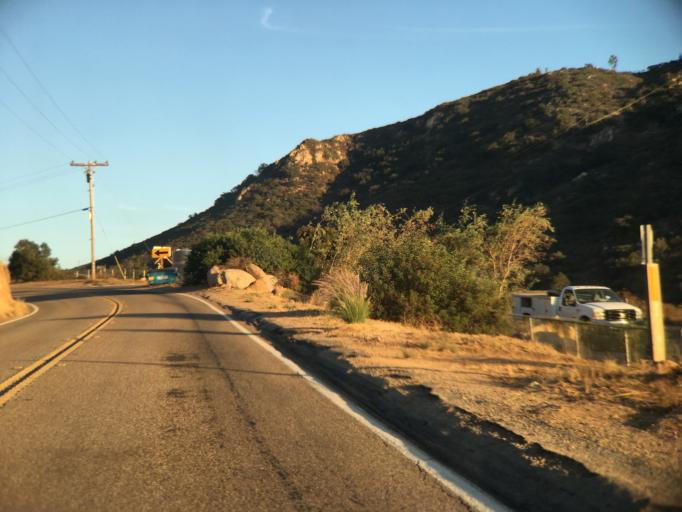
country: US
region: California
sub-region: San Diego County
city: Harbison Canyon
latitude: 32.8068
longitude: -116.7989
